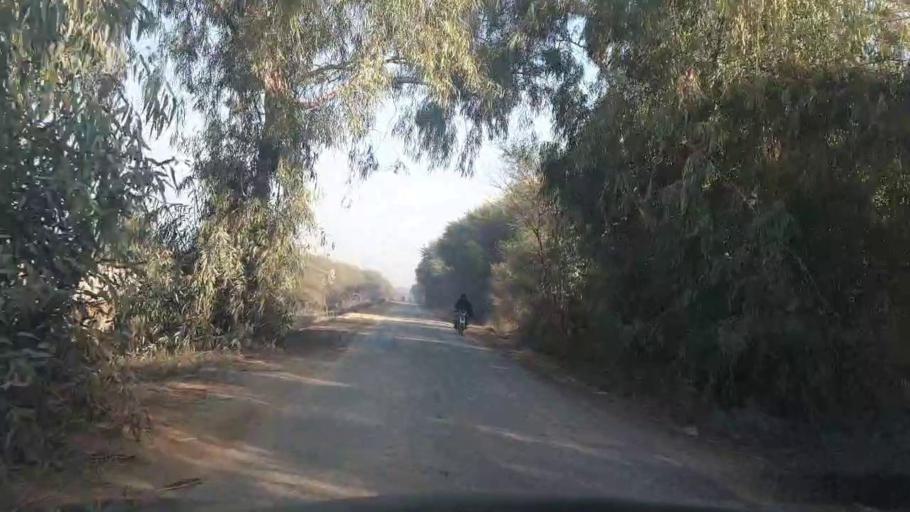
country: PK
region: Sindh
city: Mirpur Mathelo
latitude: 28.0498
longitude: 69.4605
